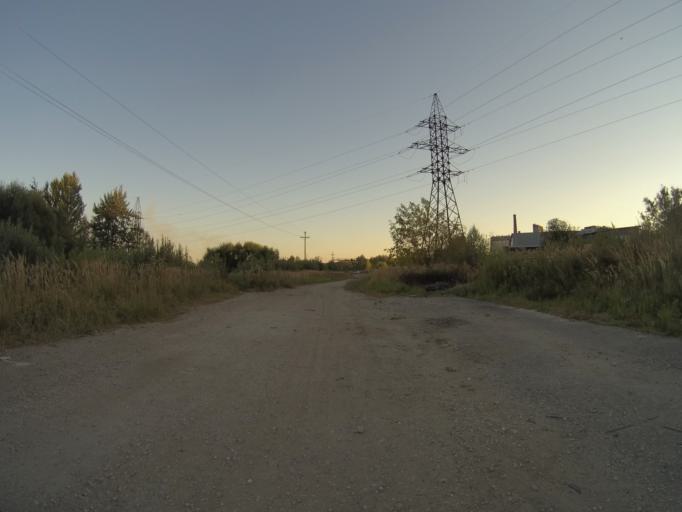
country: RU
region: Vladimir
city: Vladimir
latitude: 56.1016
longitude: 40.3737
